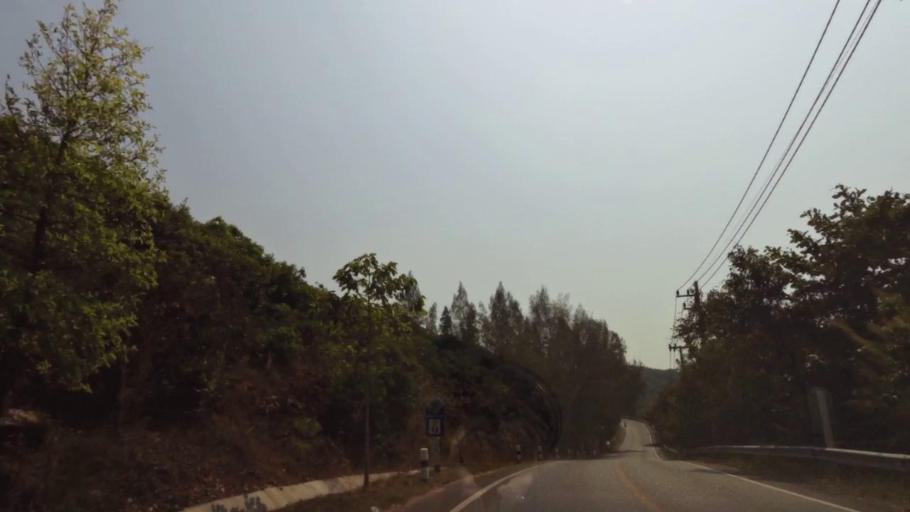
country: TH
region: Chanthaburi
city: Tha Mai
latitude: 12.5298
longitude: 101.9460
